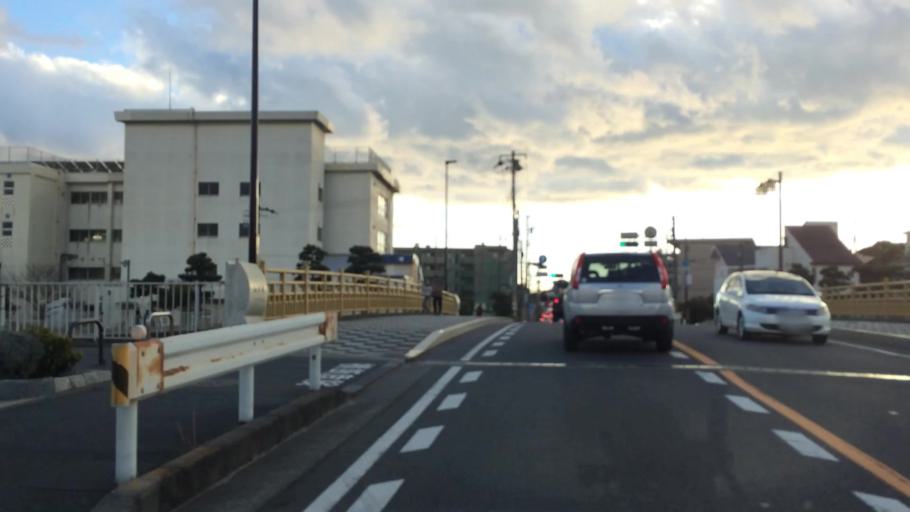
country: JP
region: Kanagawa
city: Fujisawa
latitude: 35.3196
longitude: 139.4637
